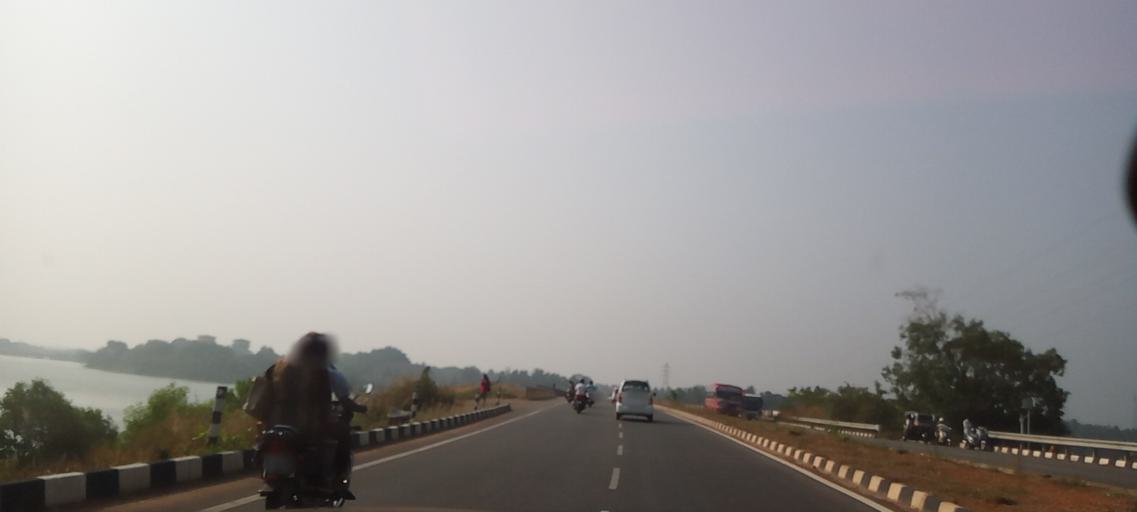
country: IN
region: Karnataka
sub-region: Udupi
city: Coondapoor
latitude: 13.6414
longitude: 74.7015
